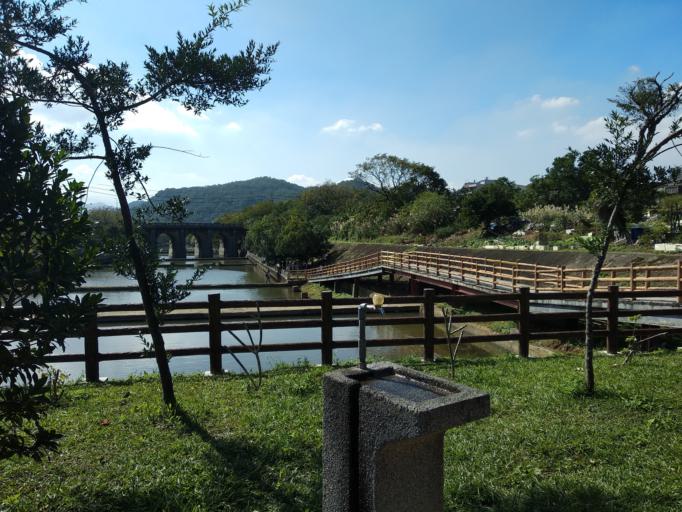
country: TW
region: Taiwan
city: Daxi
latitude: 24.7921
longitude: 121.1807
